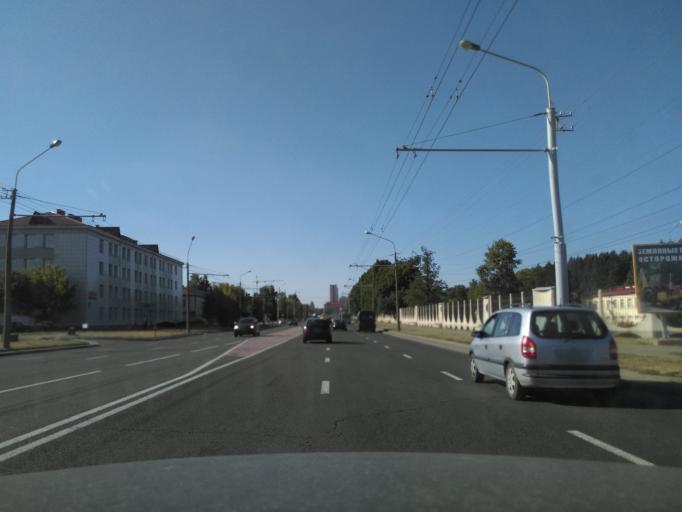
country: BY
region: Minsk
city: Minsk
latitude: 53.9085
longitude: 27.6118
